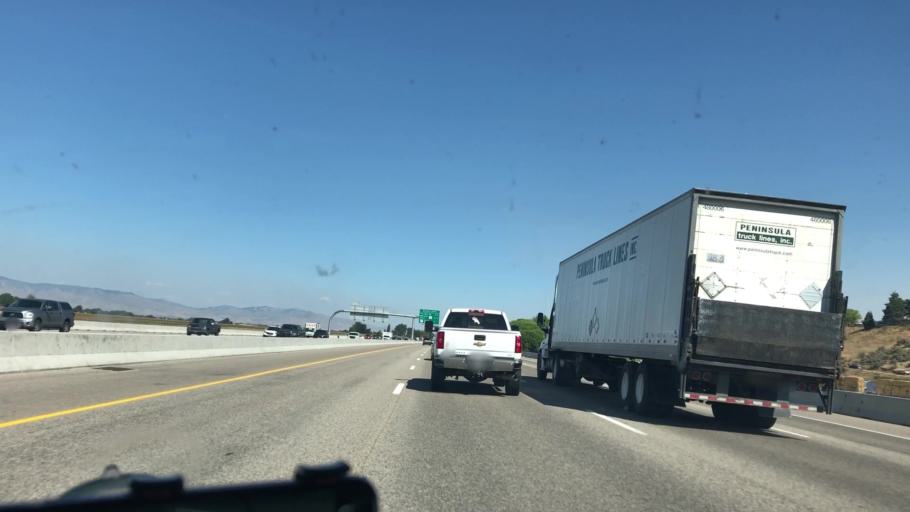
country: US
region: Idaho
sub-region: Ada County
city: Star
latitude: 43.5988
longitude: -116.4901
